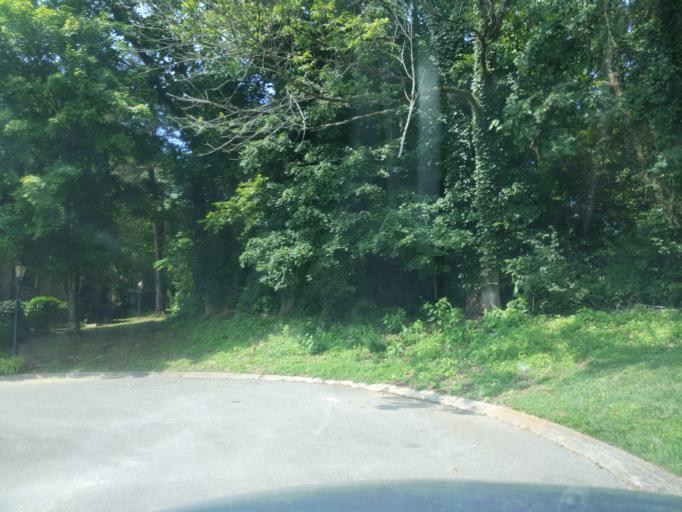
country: US
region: Tennessee
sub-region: Williamson County
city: Brentwood Estates
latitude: 36.0344
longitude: -86.7494
